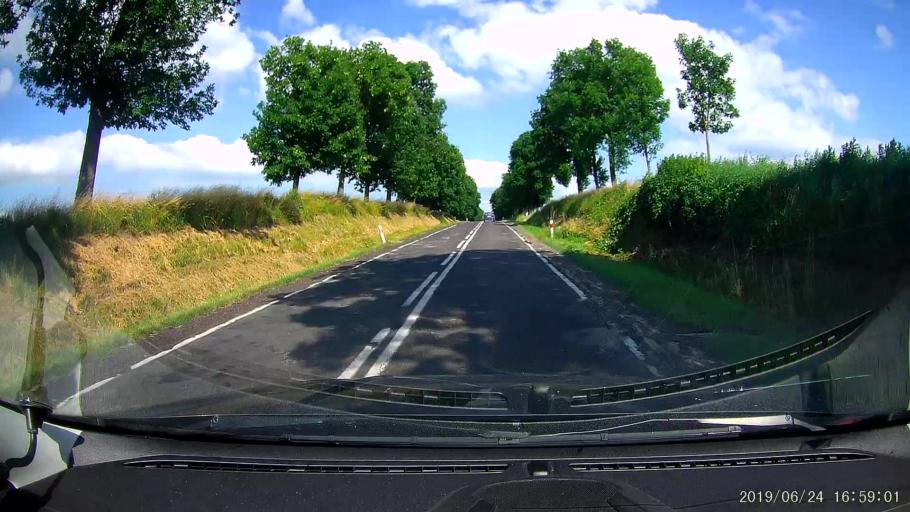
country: PL
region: Lublin Voivodeship
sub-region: Powiat tomaszowski
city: Telatyn
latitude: 50.5242
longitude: 23.8937
